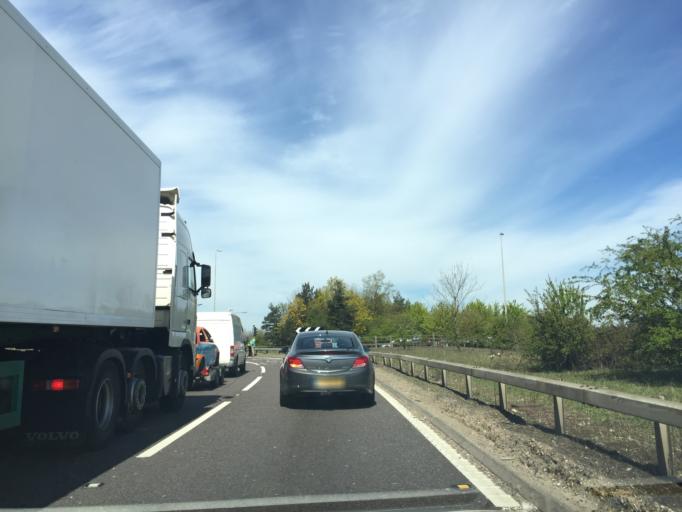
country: GB
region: England
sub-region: Essex
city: Harlow
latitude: 51.7419
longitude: 0.1365
